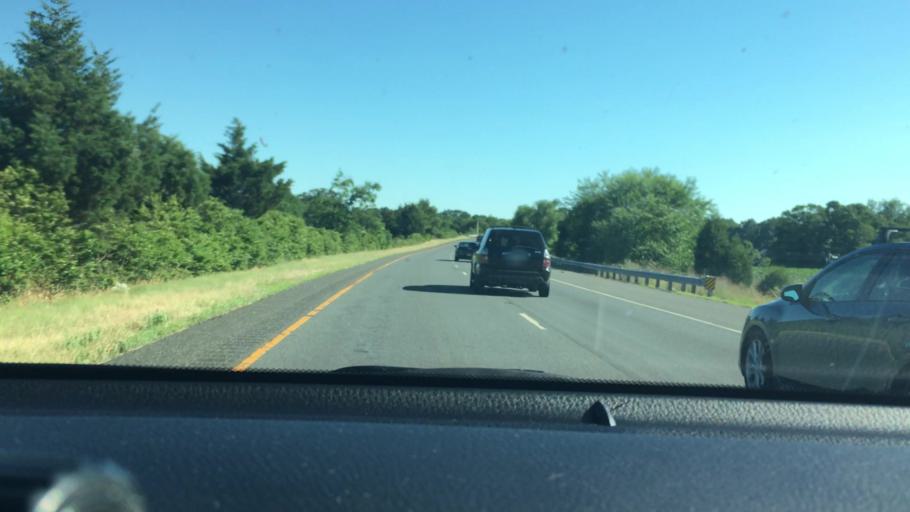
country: US
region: New Jersey
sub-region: Gloucester County
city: Newfield
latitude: 39.5513
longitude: -75.0582
